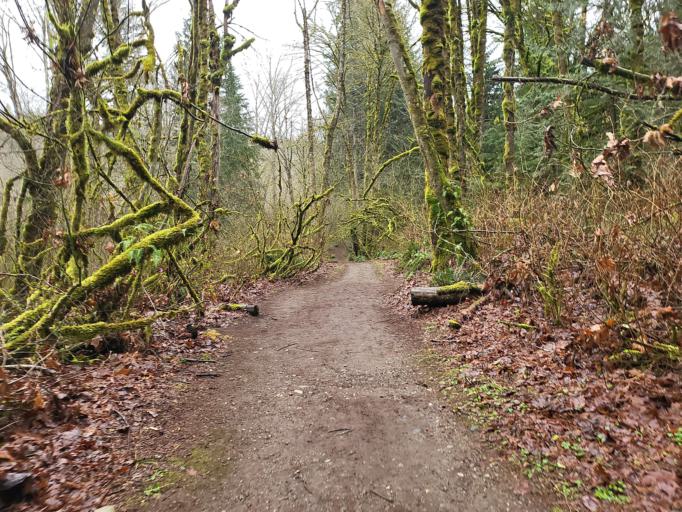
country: US
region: Washington
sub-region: King County
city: Newcastle
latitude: 47.5267
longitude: -122.1250
